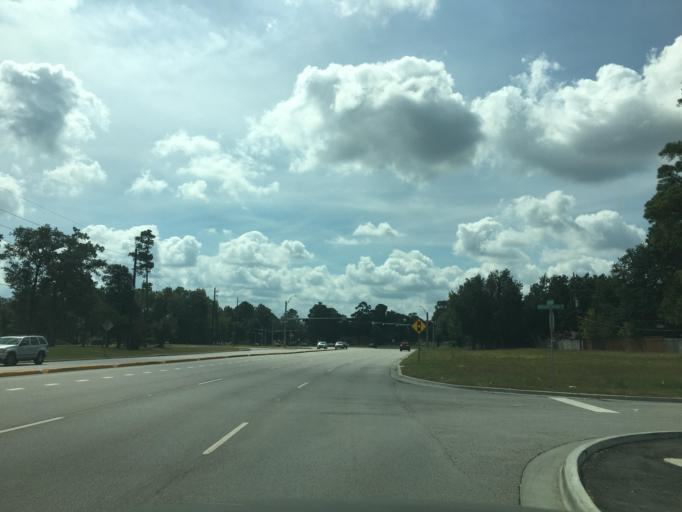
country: US
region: Texas
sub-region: Harris County
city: Spring
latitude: 30.1191
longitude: -95.3977
